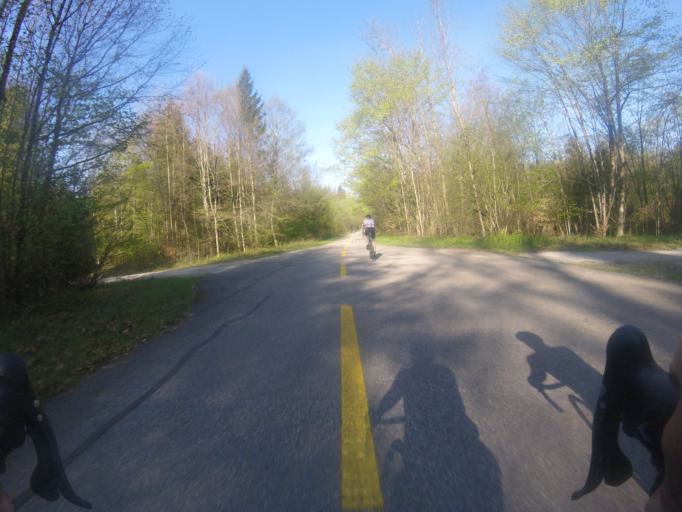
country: CH
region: Bern
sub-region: Bern-Mittelland District
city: Wohlen
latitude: 46.9641
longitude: 7.3956
